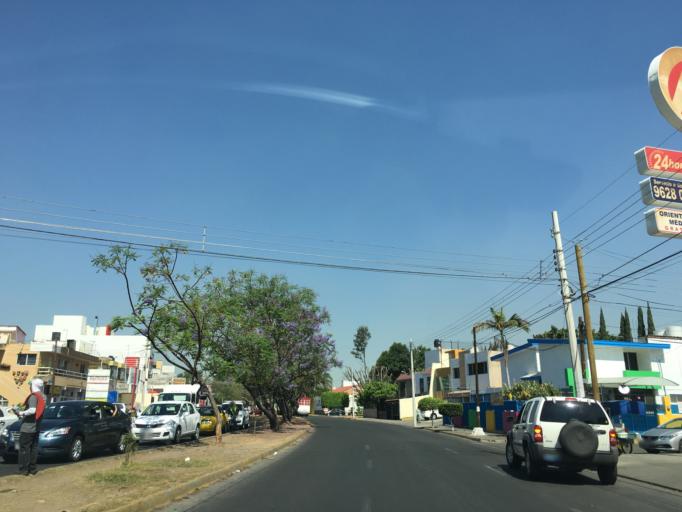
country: MX
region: Jalisco
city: Guadalajara
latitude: 20.6412
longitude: -103.3899
